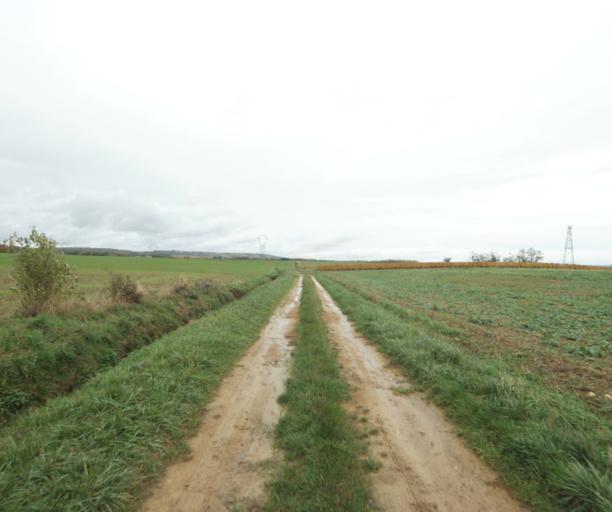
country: FR
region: Bourgogne
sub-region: Departement de Saone-et-Loire
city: Saint-Martin-Belle-Roche
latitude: 46.4650
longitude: 4.8549
